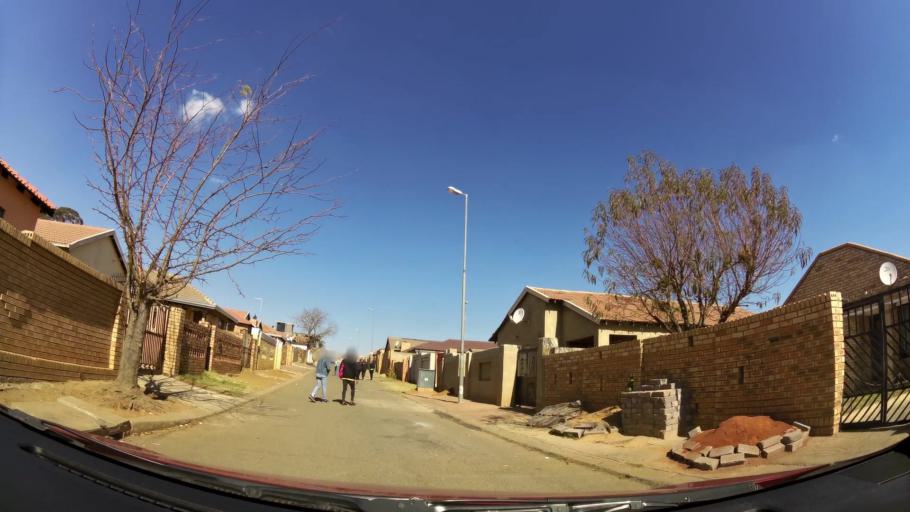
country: ZA
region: Gauteng
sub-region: City of Johannesburg Metropolitan Municipality
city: Soweto
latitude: -26.2396
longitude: 27.8167
